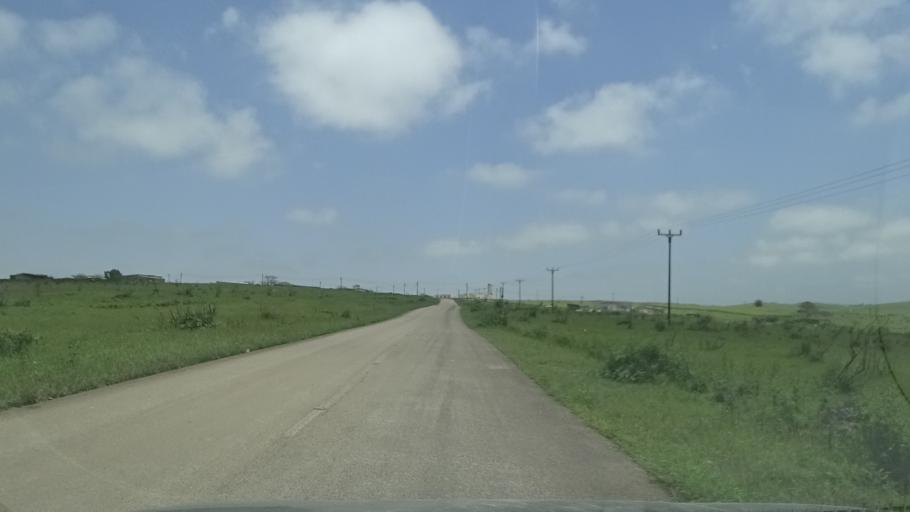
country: OM
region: Zufar
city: Salalah
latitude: 17.2282
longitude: 54.2085
